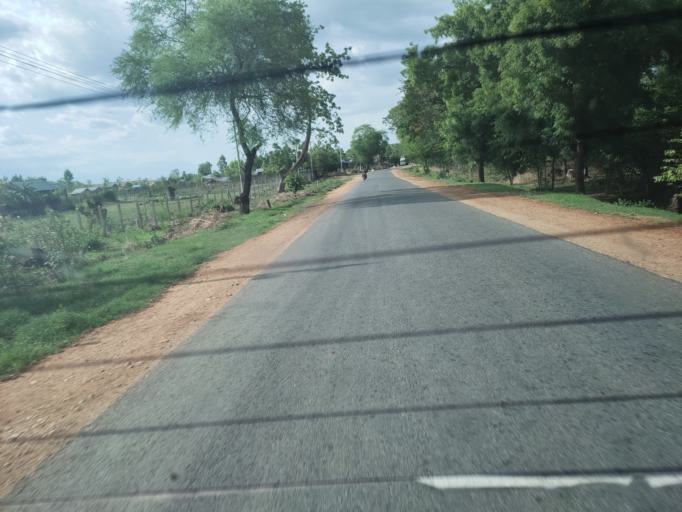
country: MM
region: Magway
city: Magway
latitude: 19.9916
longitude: 94.9881
